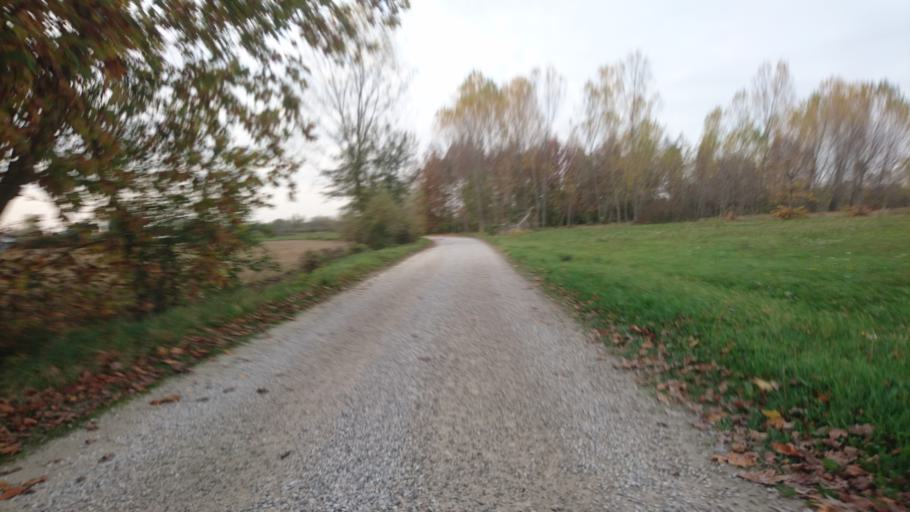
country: IT
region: Veneto
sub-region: Provincia di Padova
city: Tencarola
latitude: 45.3811
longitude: 11.8233
